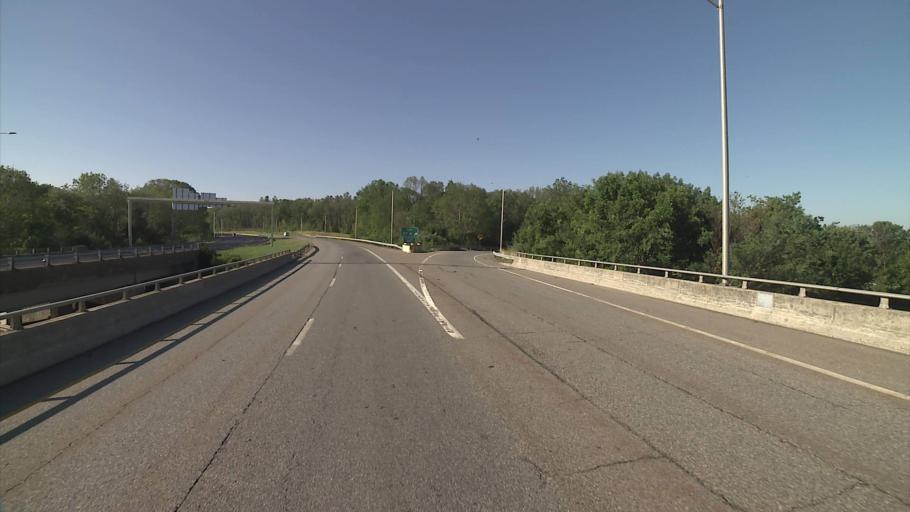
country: US
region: Connecticut
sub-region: Windham County
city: Danielson
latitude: 41.7932
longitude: -71.8769
